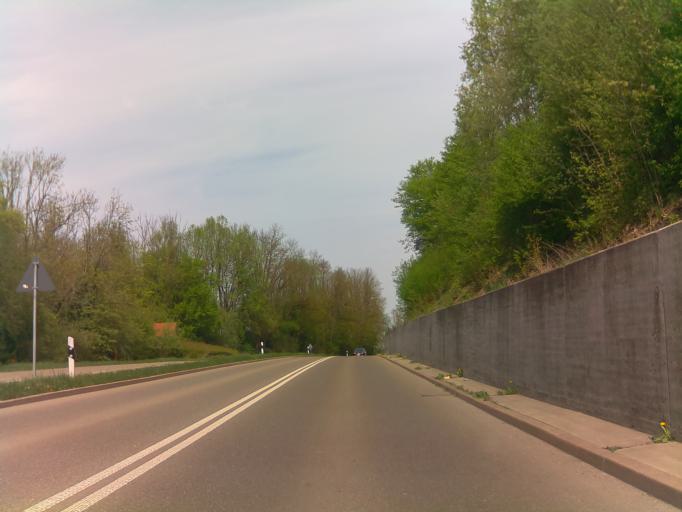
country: DE
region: Baden-Wuerttemberg
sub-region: Freiburg Region
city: Rottweil
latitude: 48.1729
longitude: 8.6300
